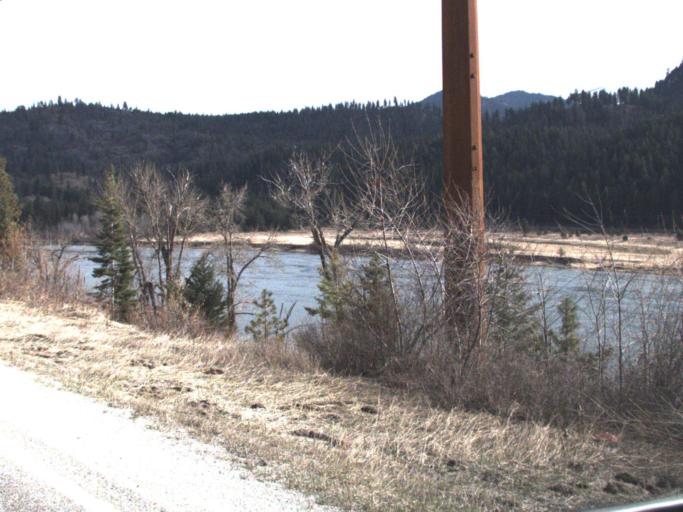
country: US
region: Washington
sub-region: Pend Oreille County
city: Newport
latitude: 48.4917
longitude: -117.2688
